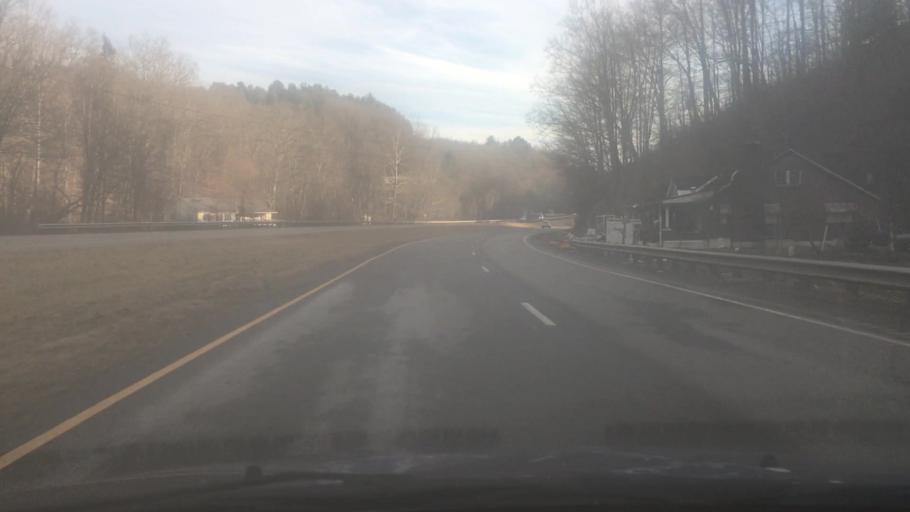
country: US
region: Virginia
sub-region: Wise County
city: Pound
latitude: 37.0871
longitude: -82.5990
